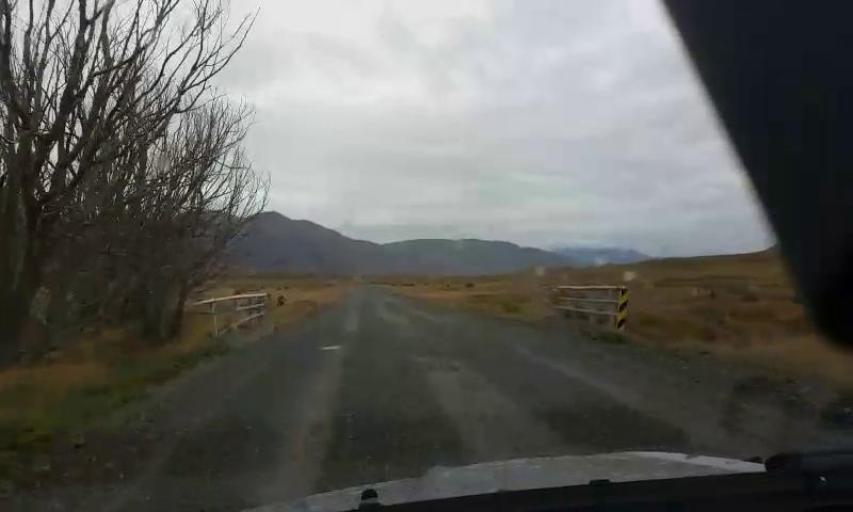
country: NZ
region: Canterbury
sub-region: Ashburton District
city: Methven
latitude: -43.6145
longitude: 171.1125
